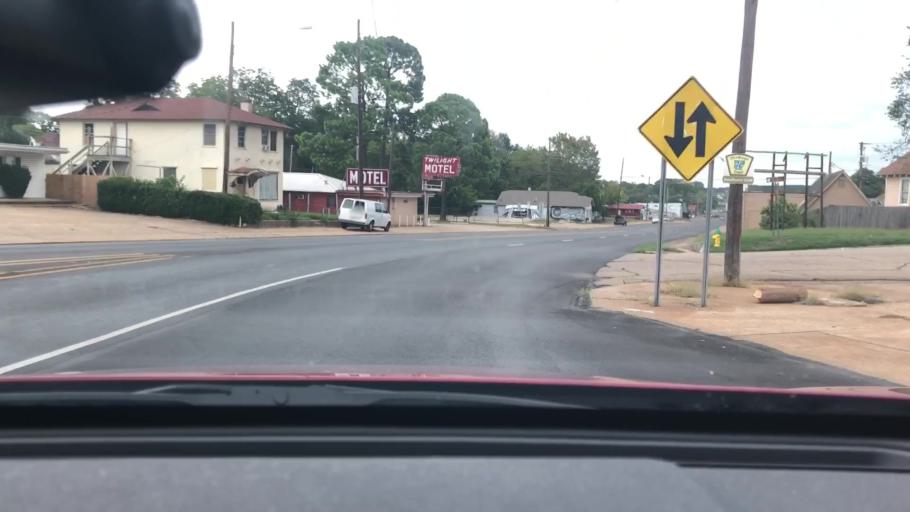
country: US
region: Arkansas
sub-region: Miller County
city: Texarkana
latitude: 33.4309
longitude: -94.0352
